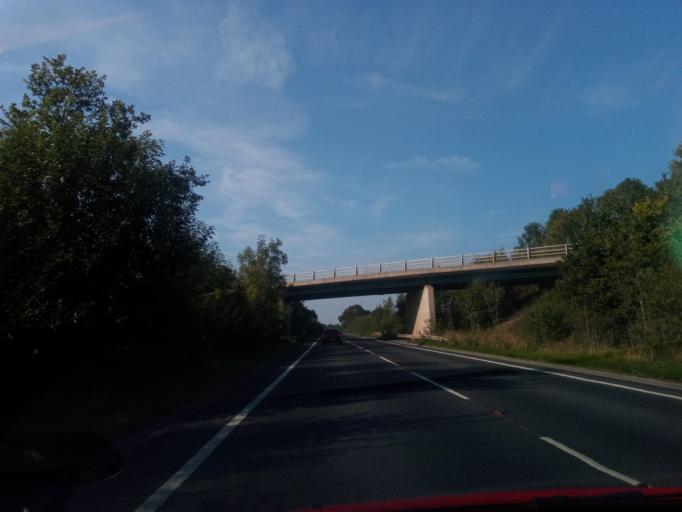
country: GB
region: England
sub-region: North Yorkshire
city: Raskelf
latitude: 54.1349
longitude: -1.2316
